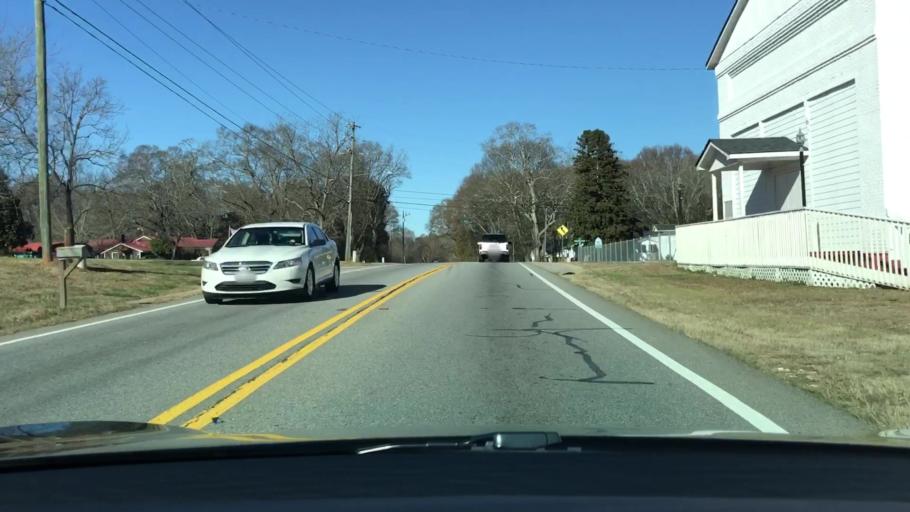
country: US
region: Georgia
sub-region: Walton County
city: Monroe
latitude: 33.8709
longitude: -83.7199
